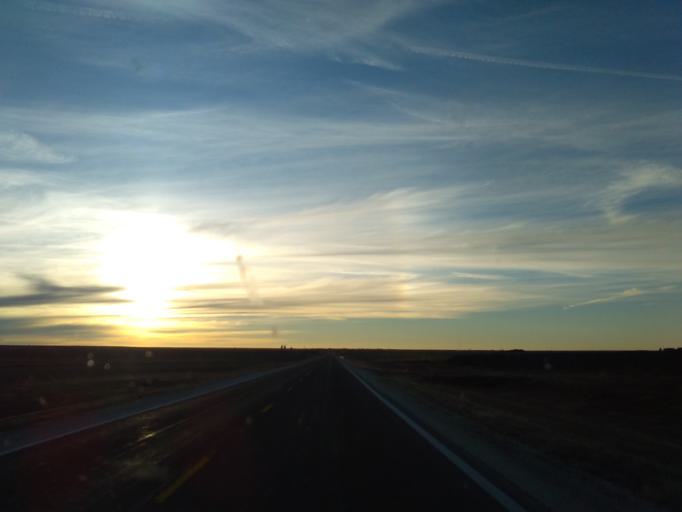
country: US
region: Kansas
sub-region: Logan County
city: Oakley
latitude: 39.0835
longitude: -101.1739
